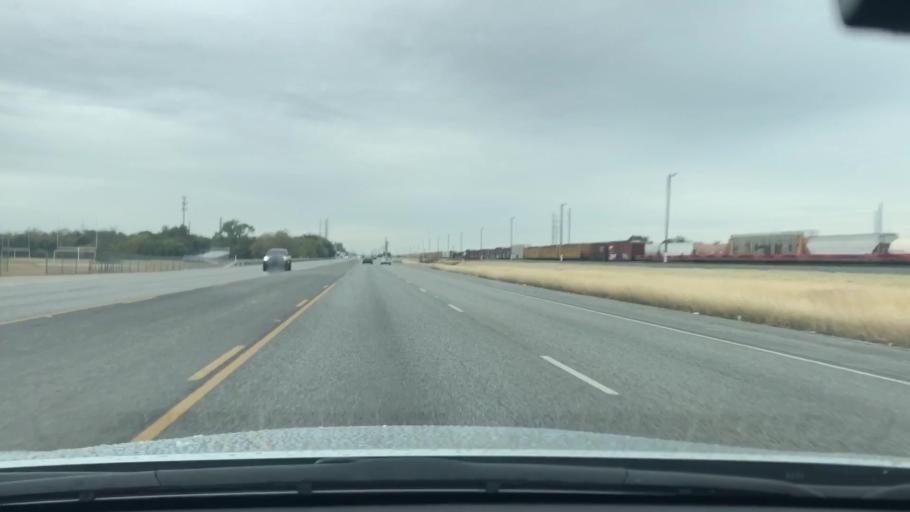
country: US
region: Texas
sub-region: Bexar County
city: Kirby
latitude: 29.4710
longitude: -98.3874
